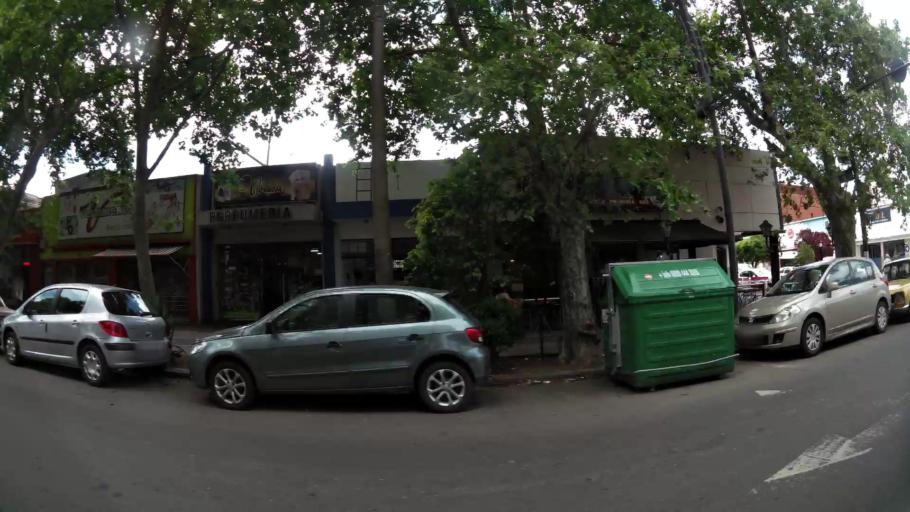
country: AR
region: Santa Fe
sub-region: Departamento de Rosario
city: Rosario
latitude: -32.9757
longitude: -60.6439
